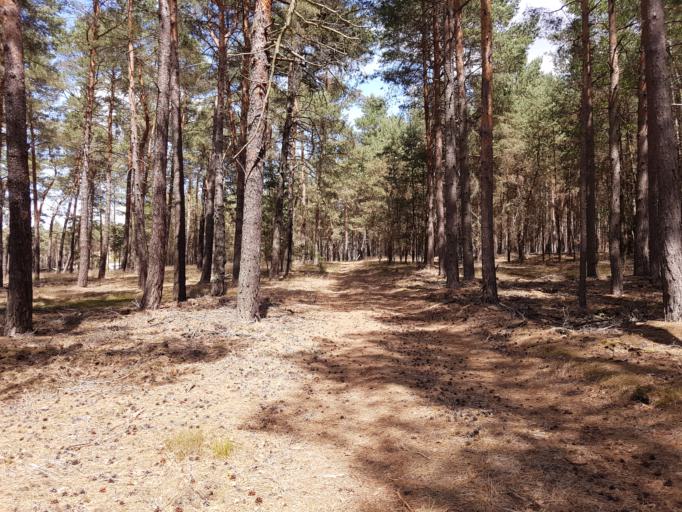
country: DE
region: Brandenburg
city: Heinersbruck
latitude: 51.7109
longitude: 14.4478
